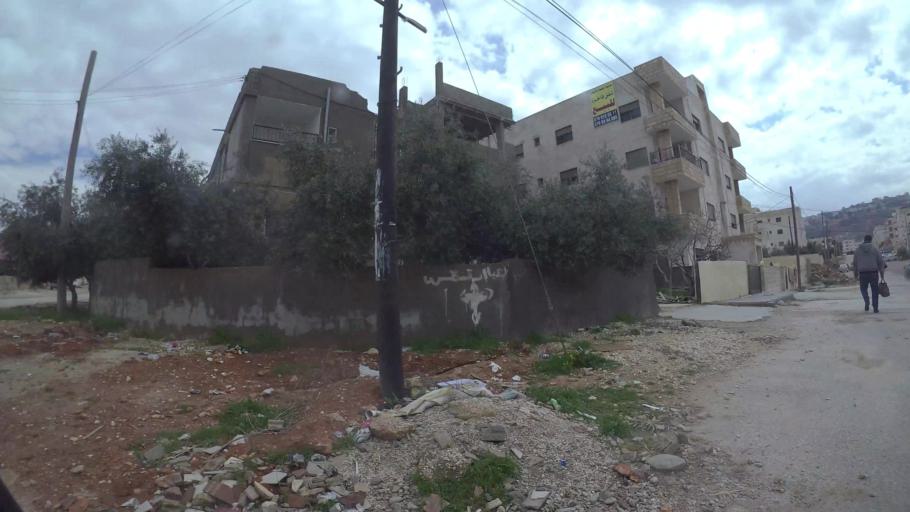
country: JO
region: Amman
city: Al Jubayhah
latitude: 32.0569
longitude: 35.8223
